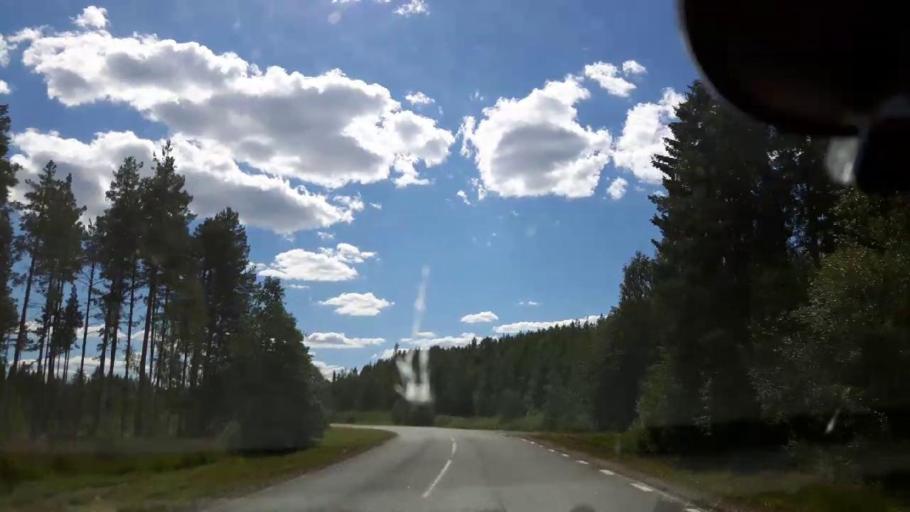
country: SE
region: Jaemtland
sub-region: Ragunda Kommun
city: Hammarstrand
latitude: 62.8687
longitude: 16.2151
